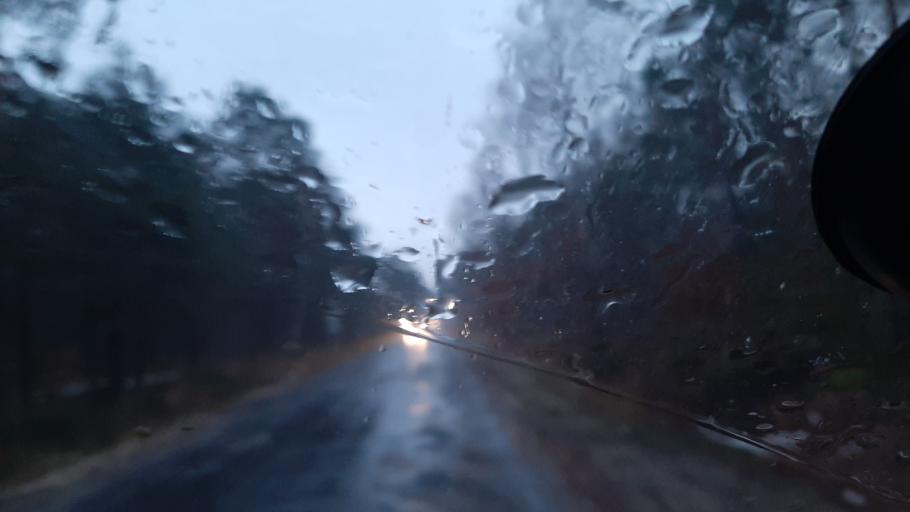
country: PL
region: Lublin Voivodeship
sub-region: Powiat lubartowski
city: Firlej
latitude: 51.5506
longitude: 22.5068
